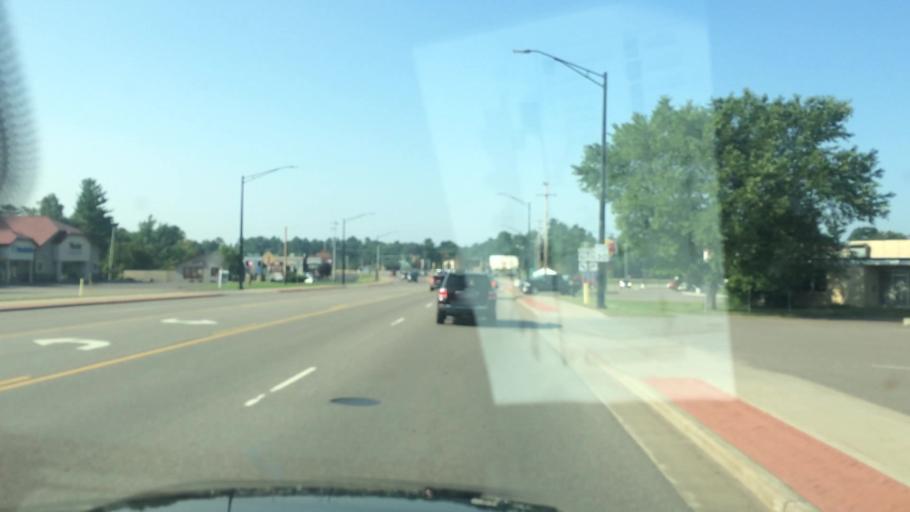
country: US
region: Wisconsin
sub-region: Vilas County
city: Lac du Flambeau
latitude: 45.8896
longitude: -89.7016
